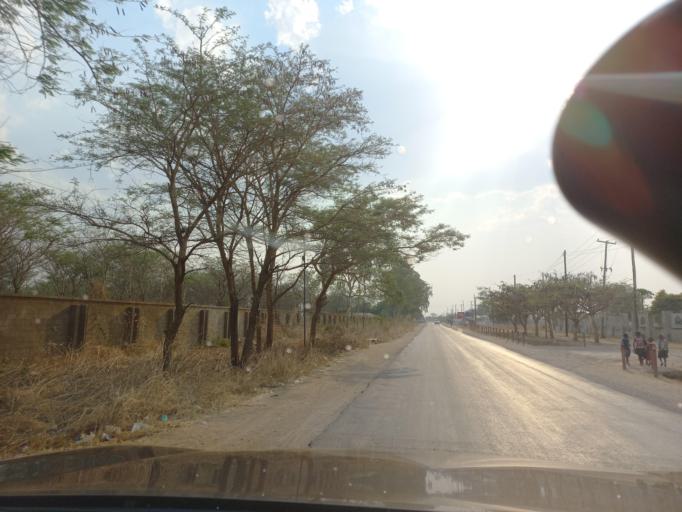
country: ZM
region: Lusaka
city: Lusaka
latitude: -15.4781
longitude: 28.2025
